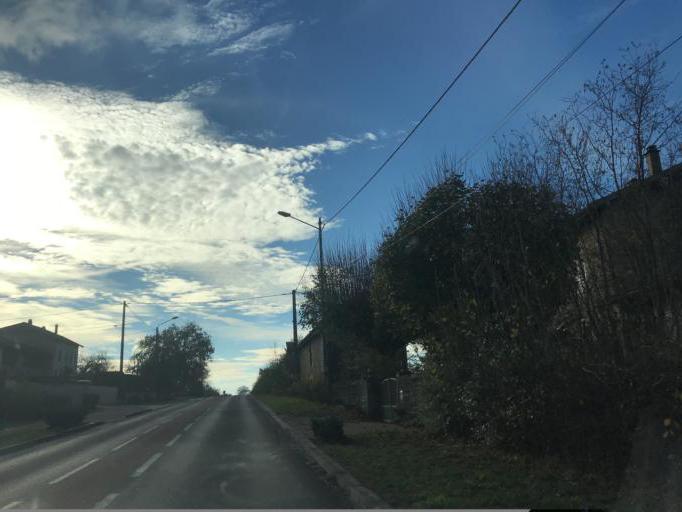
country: FR
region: Rhone-Alpes
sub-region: Departement de l'Ain
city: Saint-Jean-le-Vieux
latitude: 46.0262
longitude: 5.3853
